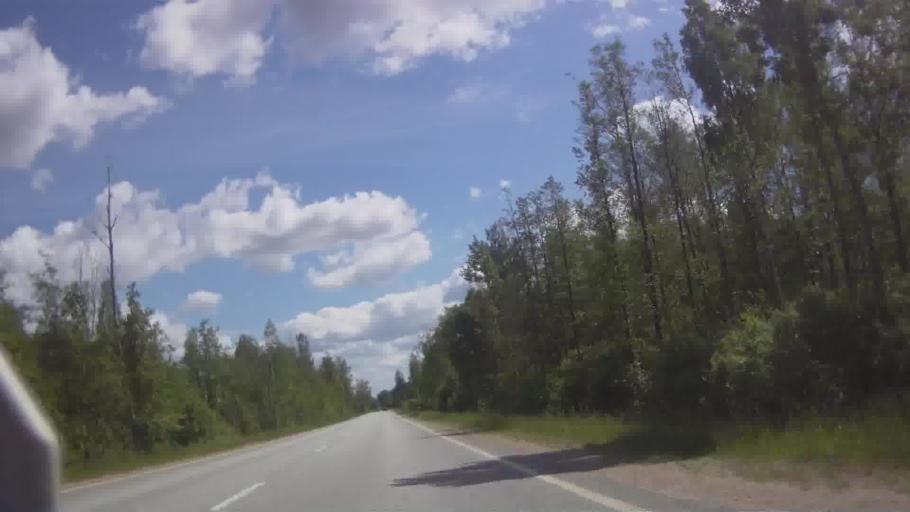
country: LV
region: Livani
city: Livani
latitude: 56.5304
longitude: 26.3583
